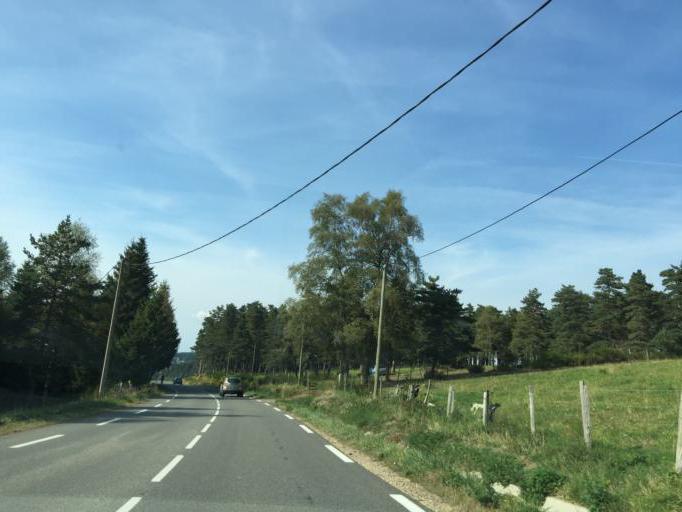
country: FR
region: Rhone-Alpes
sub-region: Departement de la Loire
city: Saint-Genest-Malifaux
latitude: 45.3752
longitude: 4.4950
